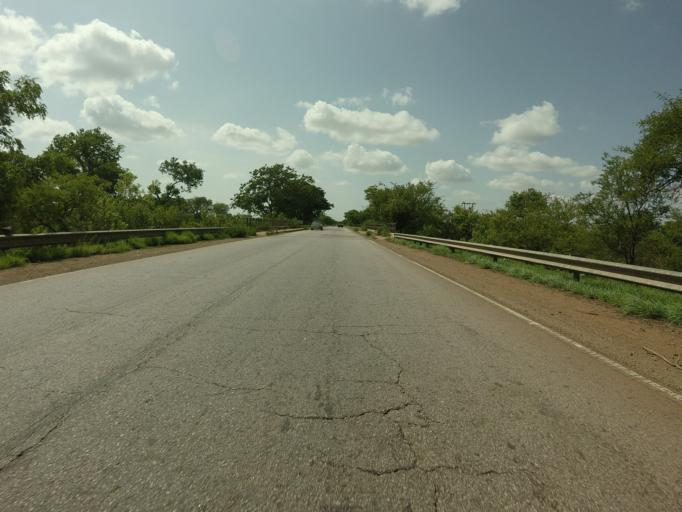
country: GH
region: Northern
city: Savelugu
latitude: 9.8297
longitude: -0.8647
